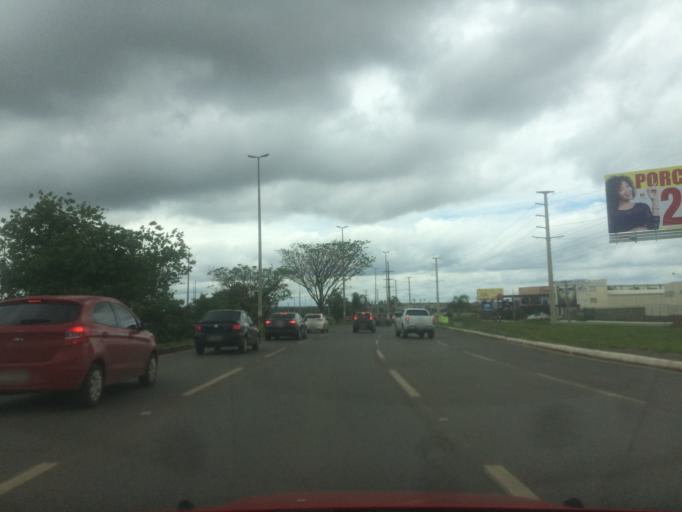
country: BR
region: Federal District
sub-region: Brasilia
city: Brasilia
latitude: -15.8506
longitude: -47.8157
